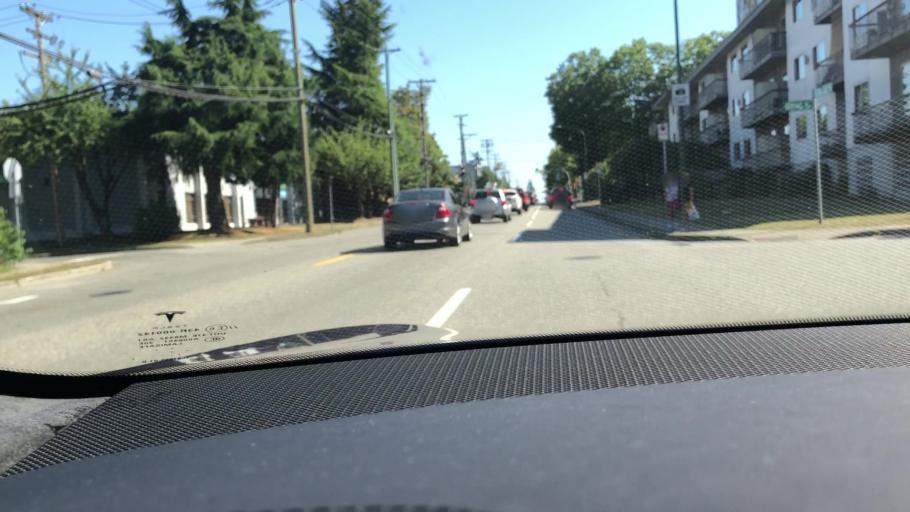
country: CA
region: British Columbia
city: Burnaby
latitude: 49.2264
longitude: -122.9890
